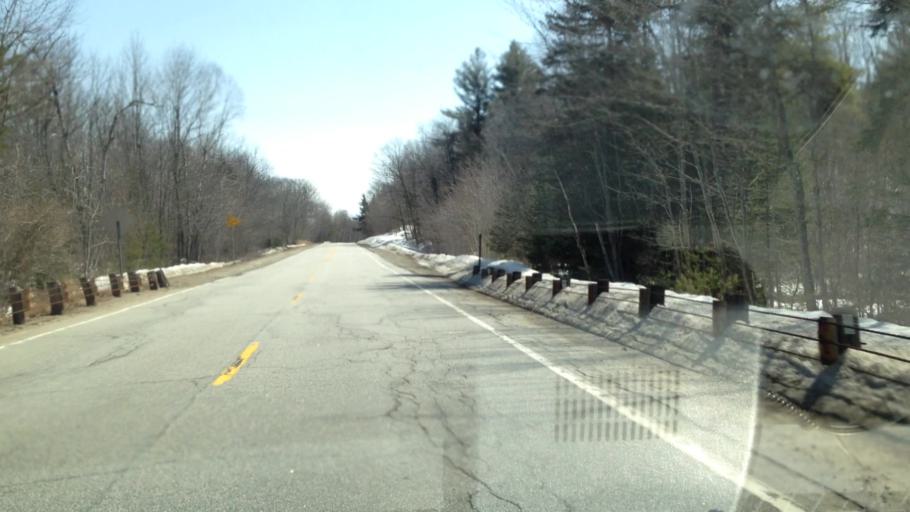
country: US
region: New Hampshire
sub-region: Sullivan County
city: Springfield
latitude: 43.4914
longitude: -71.9858
